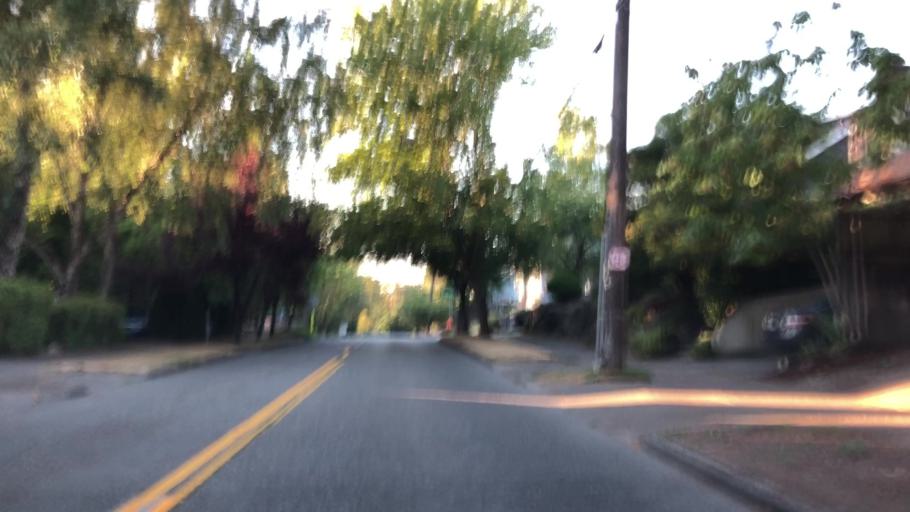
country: US
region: Washington
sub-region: King County
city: Seattle
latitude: 47.6397
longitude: -122.3073
